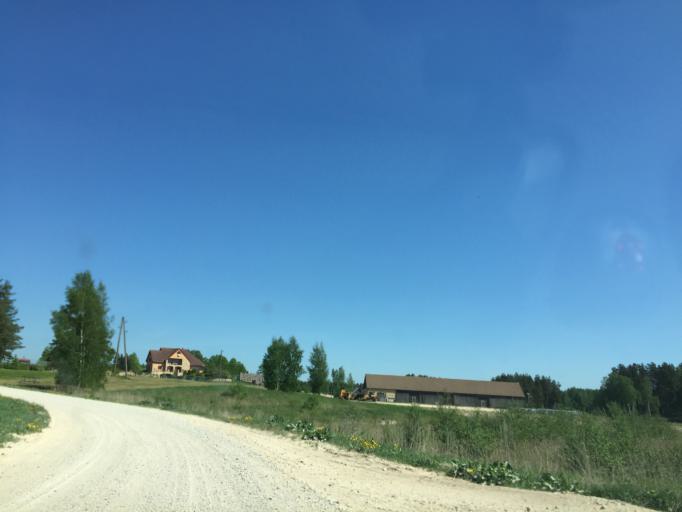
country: LV
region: Ikskile
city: Ikskile
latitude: 56.8628
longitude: 24.5014
